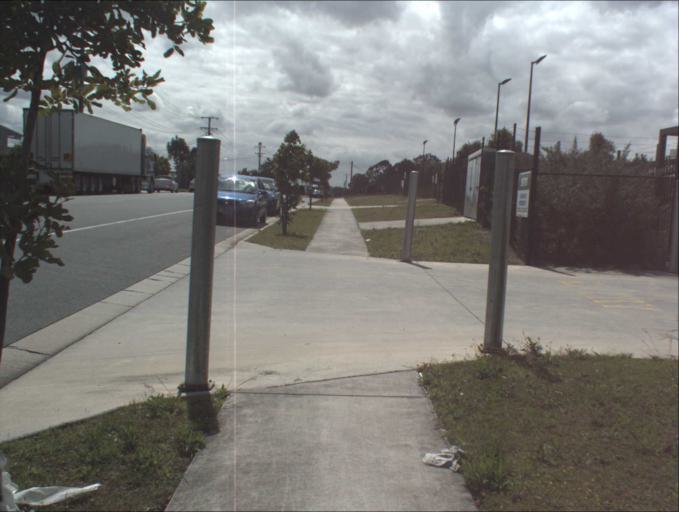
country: AU
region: Queensland
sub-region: Logan
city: Logan Reserve
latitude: -27.6859
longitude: 153.0701
